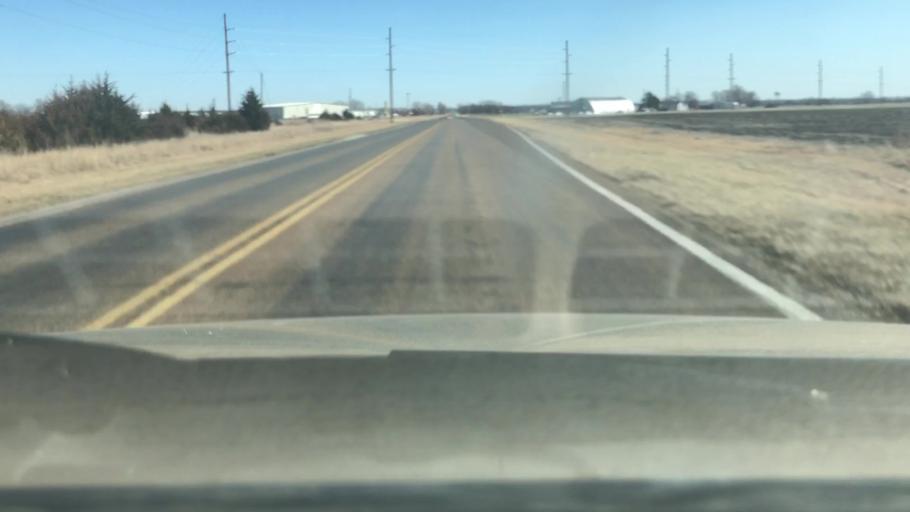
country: US
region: Kansas
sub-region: Harvey County
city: North Newton
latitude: 38.0889
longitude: -97.3737
